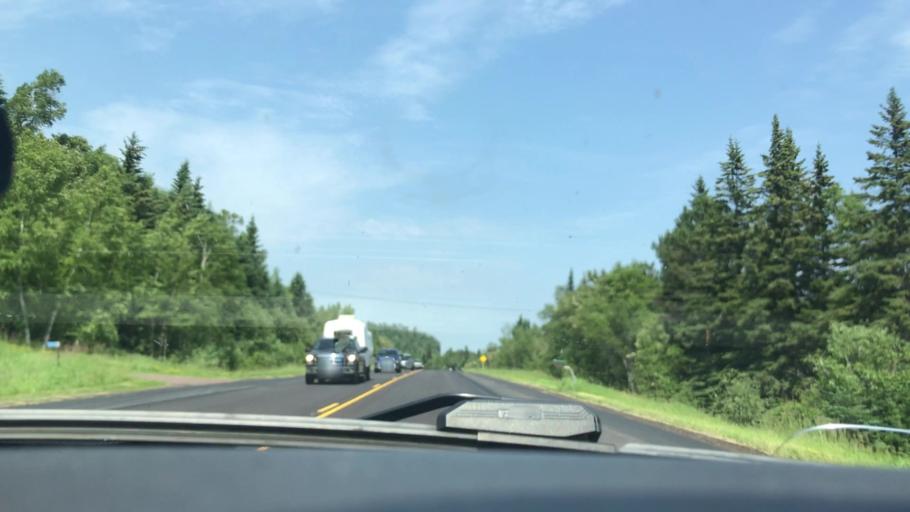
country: US
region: Minnesota
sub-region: Lake County
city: Silver Bay
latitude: 47.3591
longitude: -91.1772
